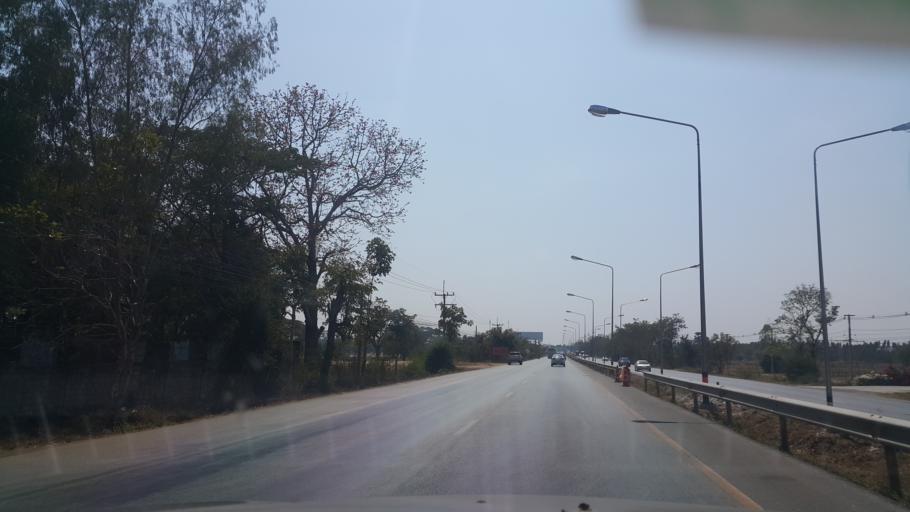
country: TH
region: Khon Kaen
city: Non Sila
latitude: 15.9762
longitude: 102.6945
